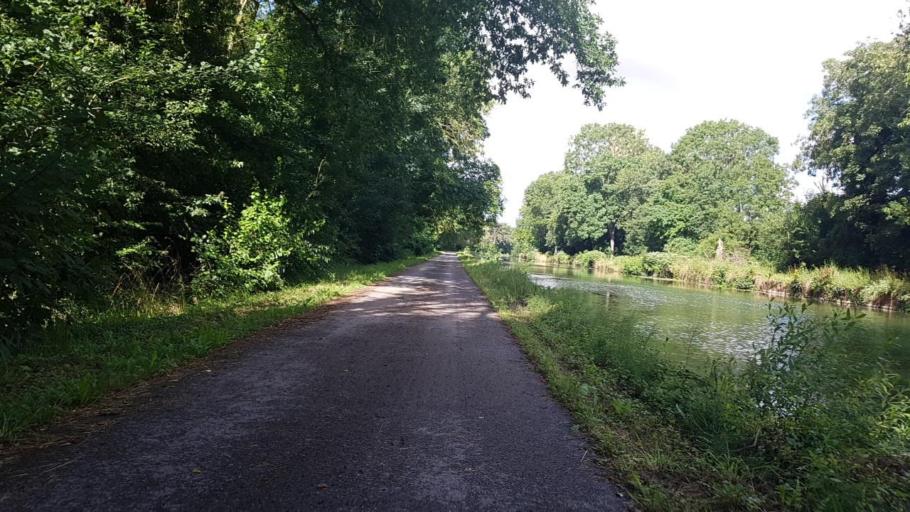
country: FR
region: Champagne-Ardenne
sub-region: Departement de la Marne
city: Tours-sur-Marne
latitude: 49.0456
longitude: 4.1333
